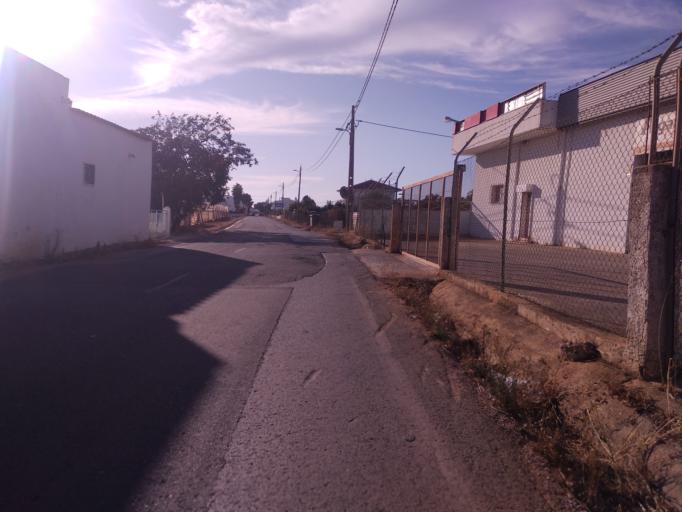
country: PT
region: Faro
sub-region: Faro
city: Faro
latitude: 37.0514
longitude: -7.9300
